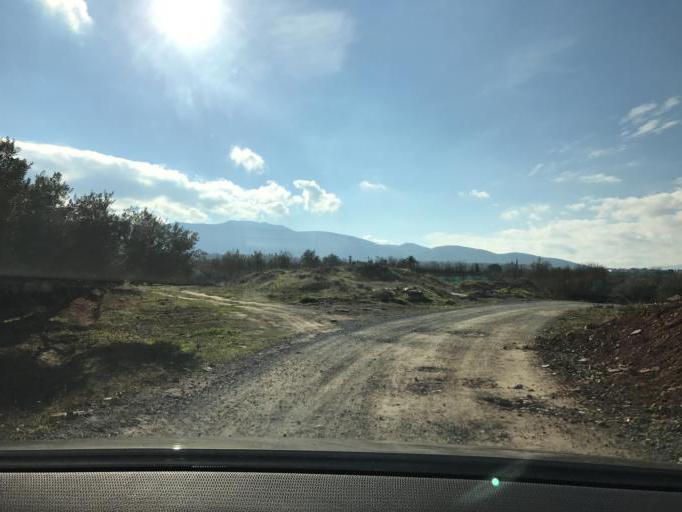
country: ES
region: Andalusia
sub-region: Provincia de Granada
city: Gojar
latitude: 37.1075
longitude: -3.6247
